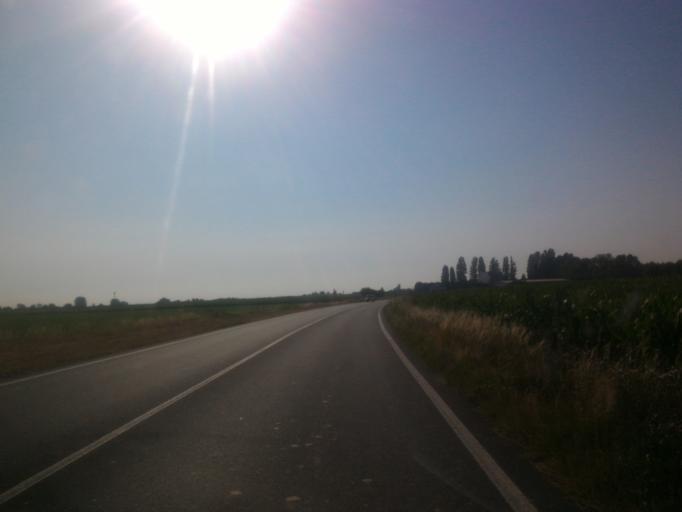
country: IT
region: Piedmont
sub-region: Provincia di Torino
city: Riva
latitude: 44.8782
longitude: 7.3763
